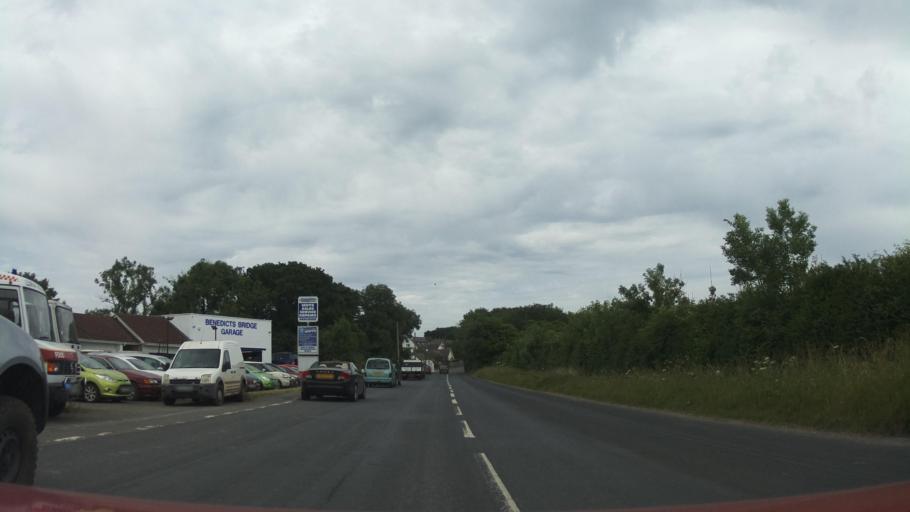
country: GB
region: England
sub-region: Devon
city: Bovey Tracey
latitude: 50.5583
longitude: -3.6724
